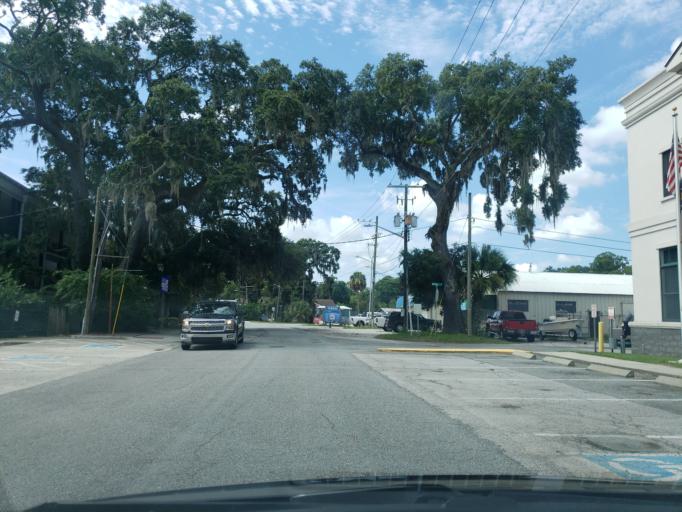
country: US
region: Georgia
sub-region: Chatham County
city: Thunderbolt
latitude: 32.0313
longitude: -81.0507
